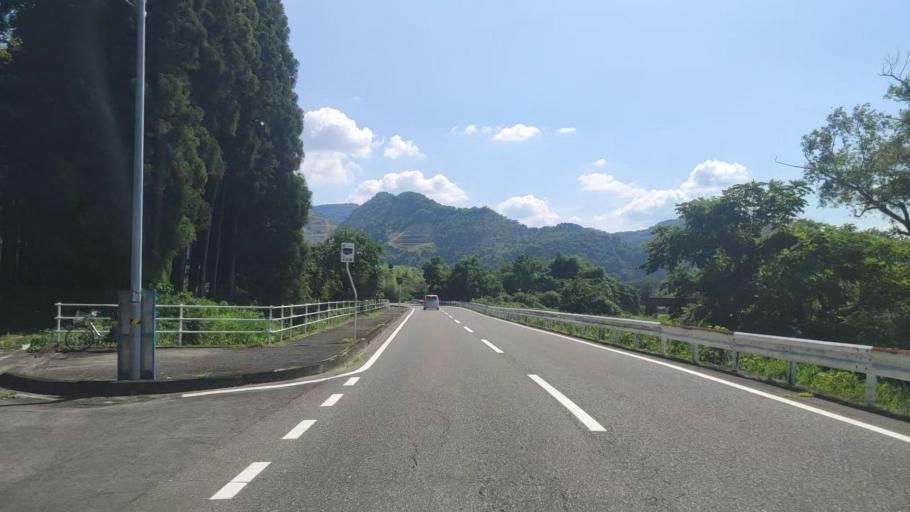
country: JP
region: Gifu
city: Godo
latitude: 35.5243
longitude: 136.6443
